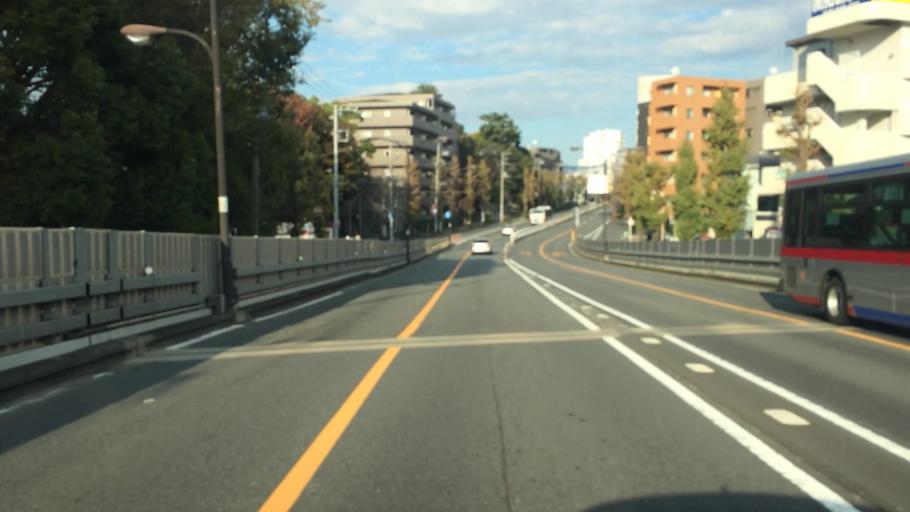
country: JP
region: Tokyo
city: Tokyo
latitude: 35.6092
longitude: 139.6499
